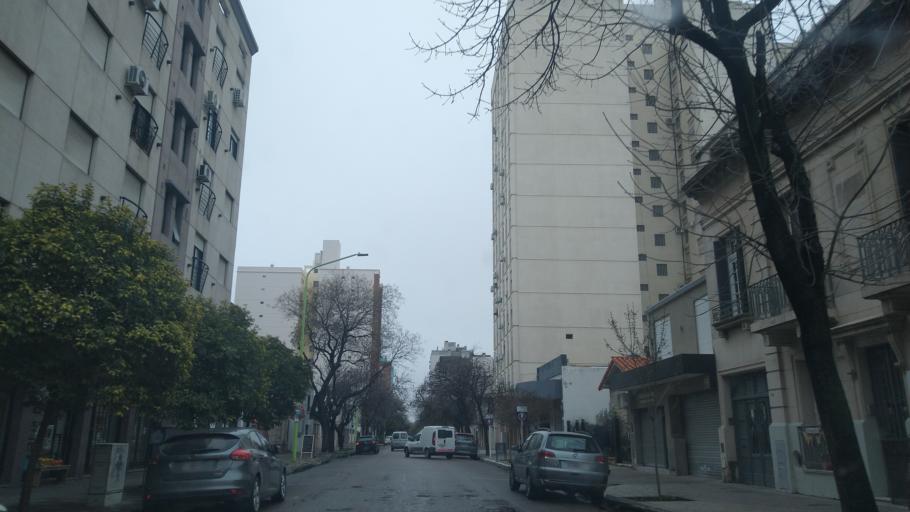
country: AR
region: Buenos Aires
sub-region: Partido de Bahia Blanca
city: Bahia Blanca
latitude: -38.7148
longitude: -62.2706
